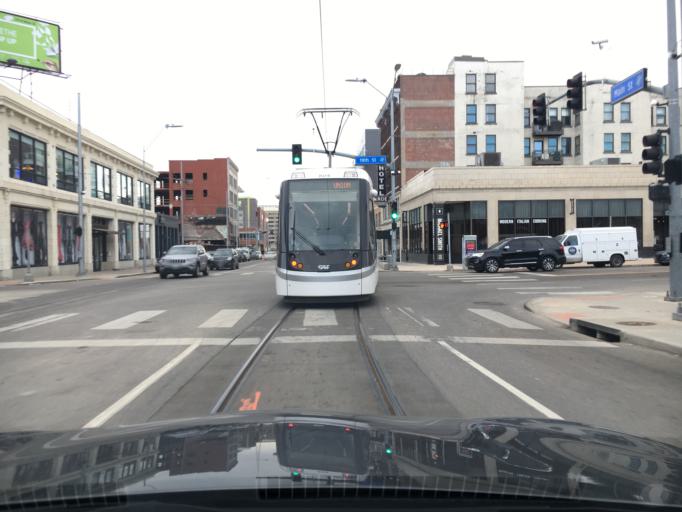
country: US
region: Missouri
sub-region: Jackson County
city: Kansas City
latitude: 39.0906
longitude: -94.5837
